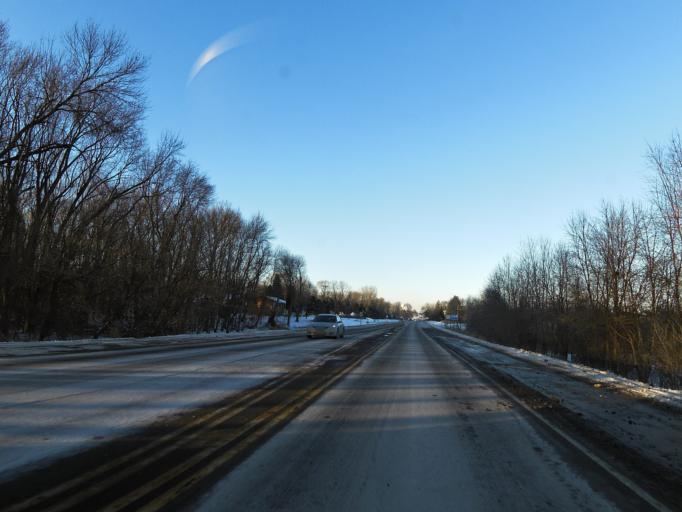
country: US
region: Minnesota
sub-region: Dakota County
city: Farmington
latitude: 44.6503
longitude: -93.1367
